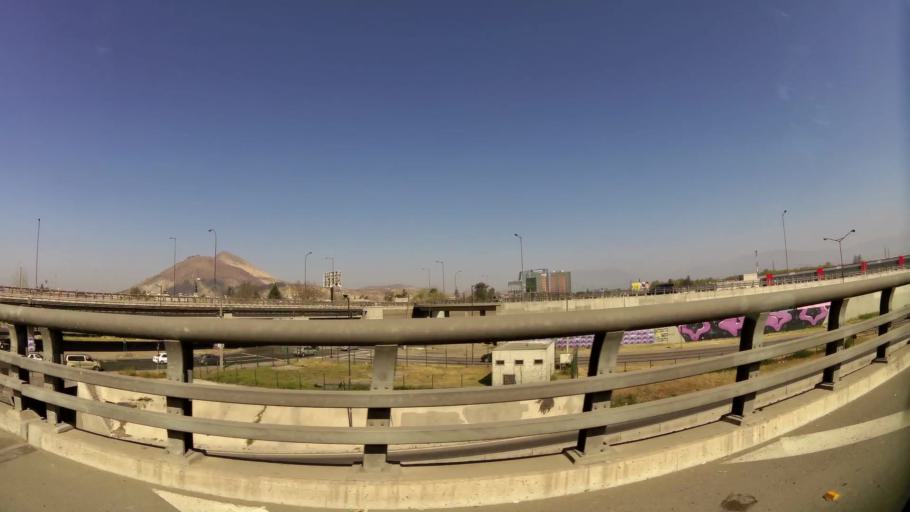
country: CL
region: Santiago Metropolitan
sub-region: Provincia de Santiago
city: Lo Prado
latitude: -33.3654
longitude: -70.6893
